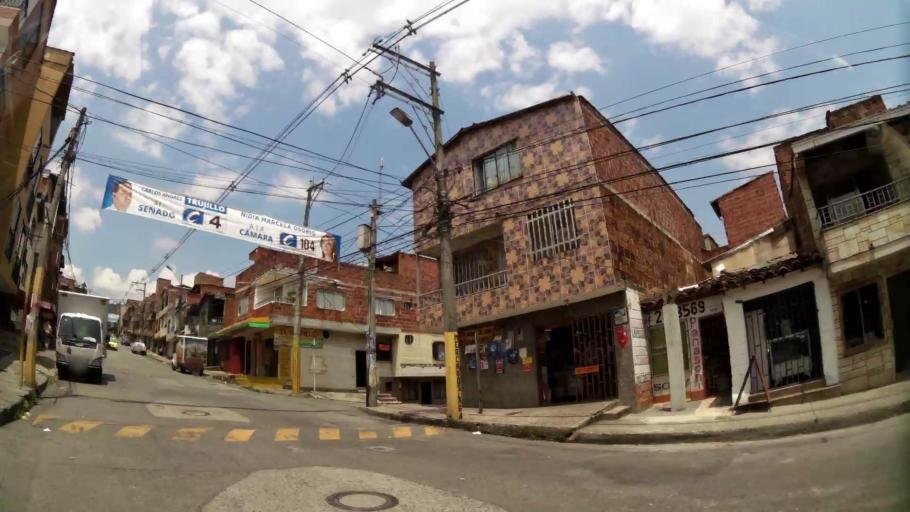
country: CO
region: Antioquia
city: Itagui
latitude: 6.1813
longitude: -75.6031
